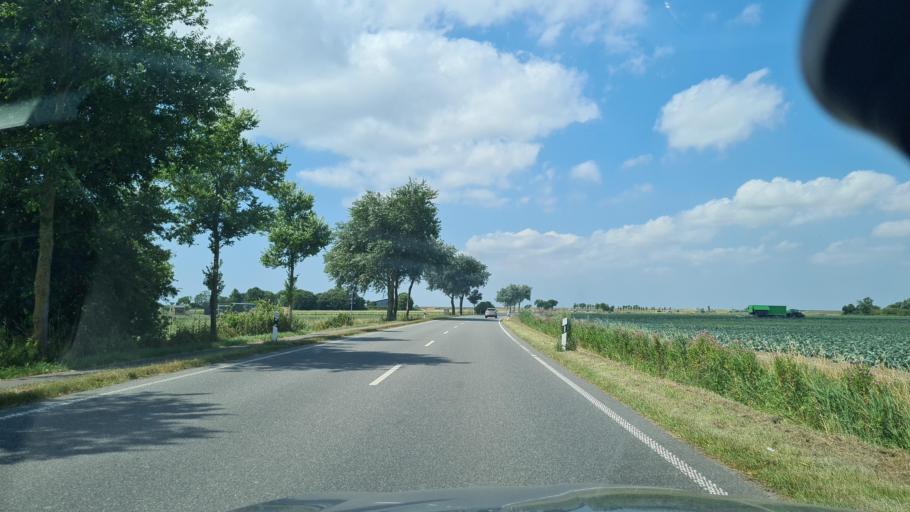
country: DE
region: Schleswig-Holstein
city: Wesselburenerkoog
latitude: 54.2457
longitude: 8.8594
